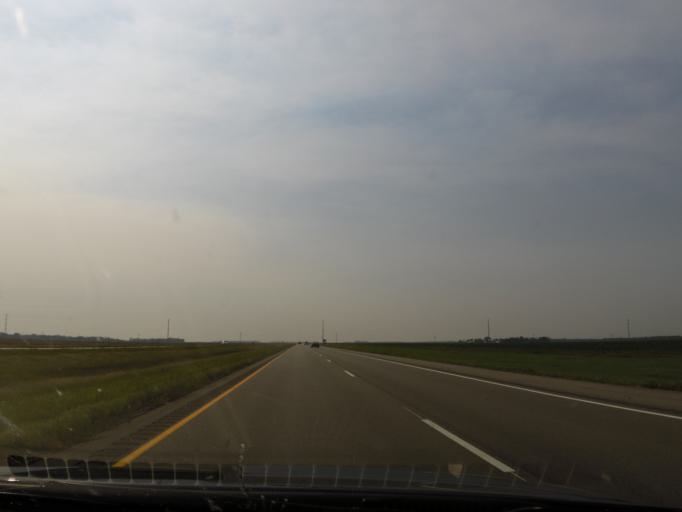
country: US
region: North Dakota
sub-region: Cass County
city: Horace
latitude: 46.6942
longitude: -96.8308
